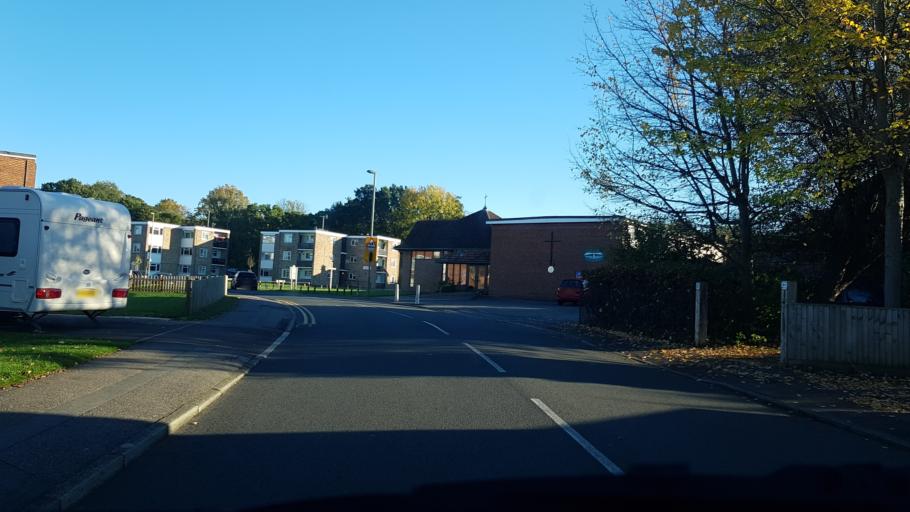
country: GB
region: England
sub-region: Surrey
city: Guildford
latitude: 51.2442
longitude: -0.6119
